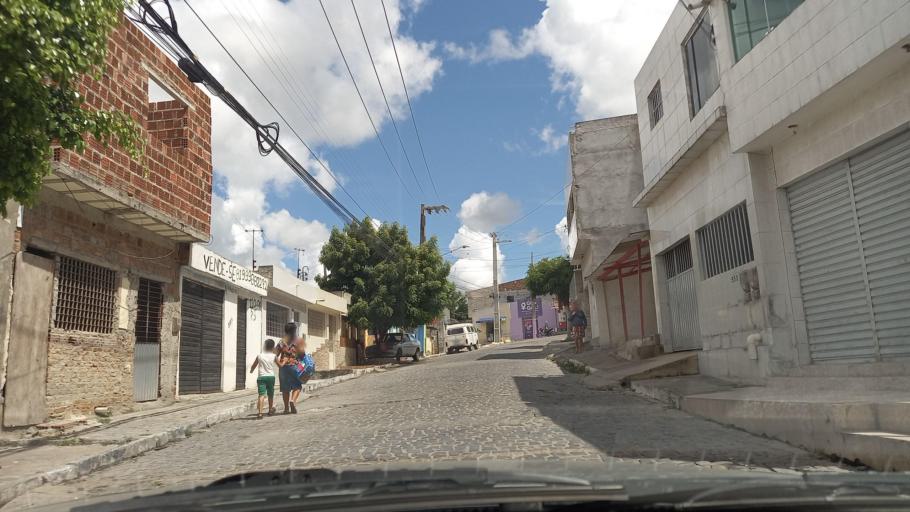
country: BR
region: Pernambuco
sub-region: Caruaru
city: Caruaru
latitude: -8.2992
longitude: -35.9717
